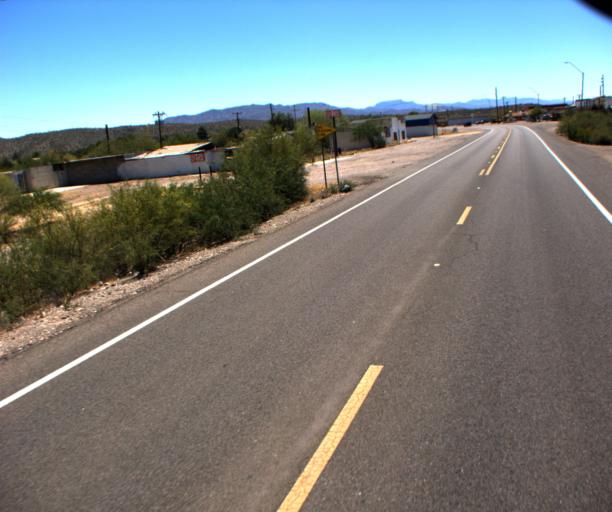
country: US
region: Arizona
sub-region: Pinal County
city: Kearny
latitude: 32.9897
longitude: -110.7787
